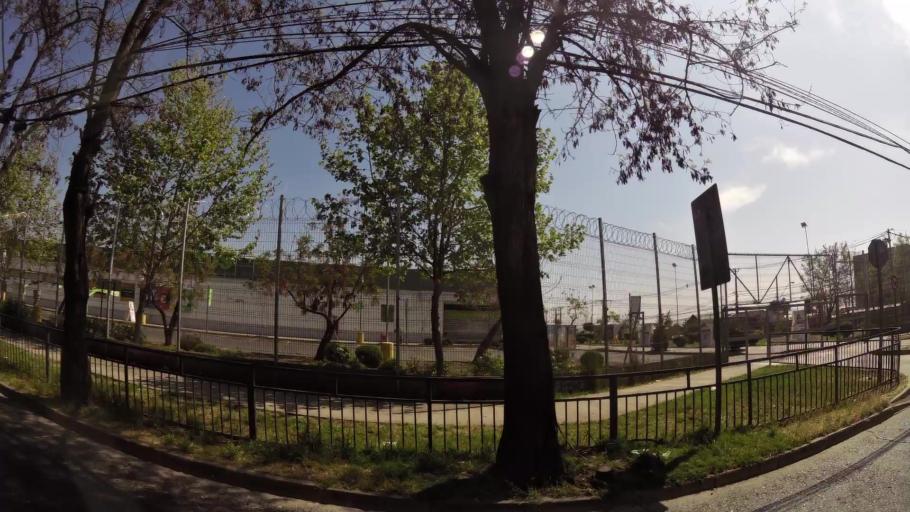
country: CL
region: Santiago Metropolitan
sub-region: Provincia de Santiago
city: Villa Presidente Frei, Nunoa, Santiago, Chile
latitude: -33.4720
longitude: -70.5544
